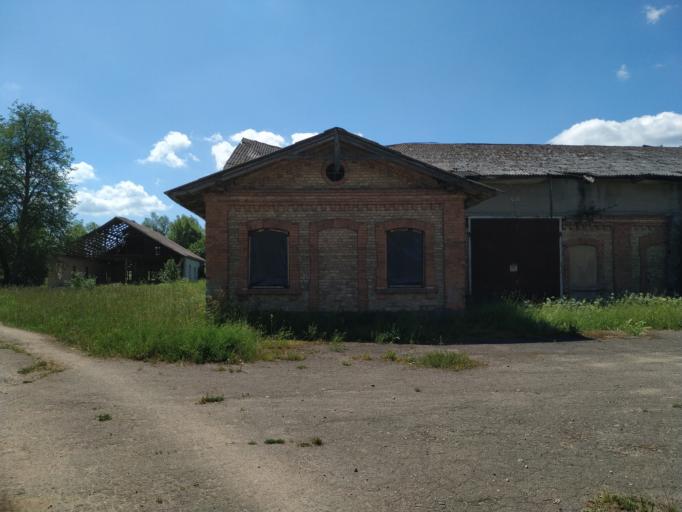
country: LT
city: Nemencine
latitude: 54.8713
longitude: 25.5401
